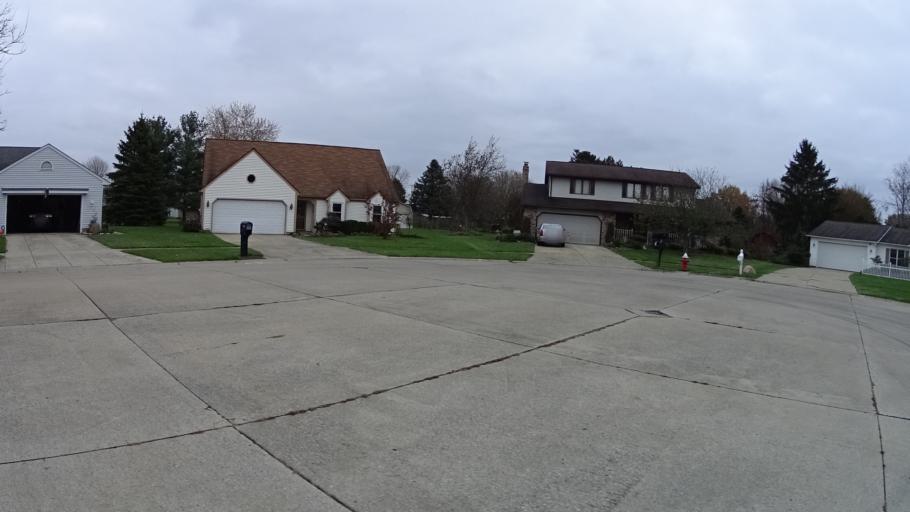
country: US
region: Ohio
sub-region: Lorain County
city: Sheffield
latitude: 41.4152
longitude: -82.0841
